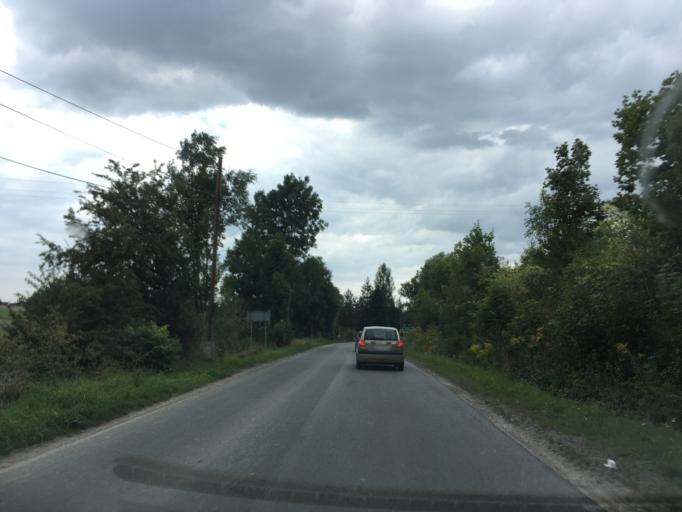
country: PL
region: Lesser Poland Voivodeship
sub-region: Powiat olkuski
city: Wolbrom
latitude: 50.3949
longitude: 19.7640
